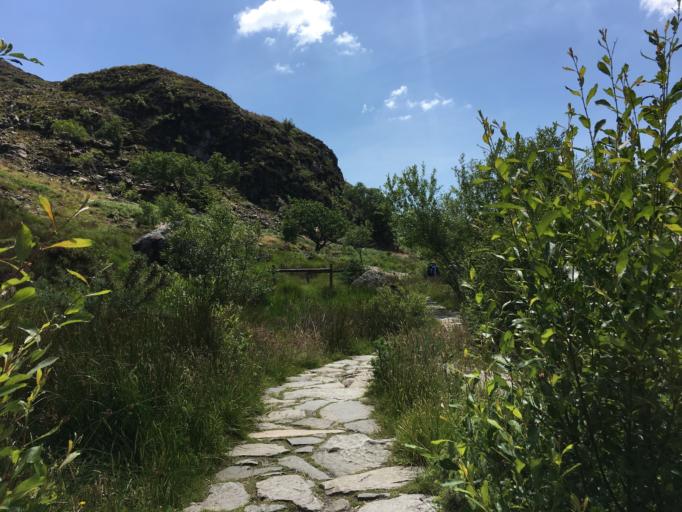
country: GB
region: Wales
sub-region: Gwynedd
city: Penrhyndeudraeth
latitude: 53.0136
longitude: -4.0987
